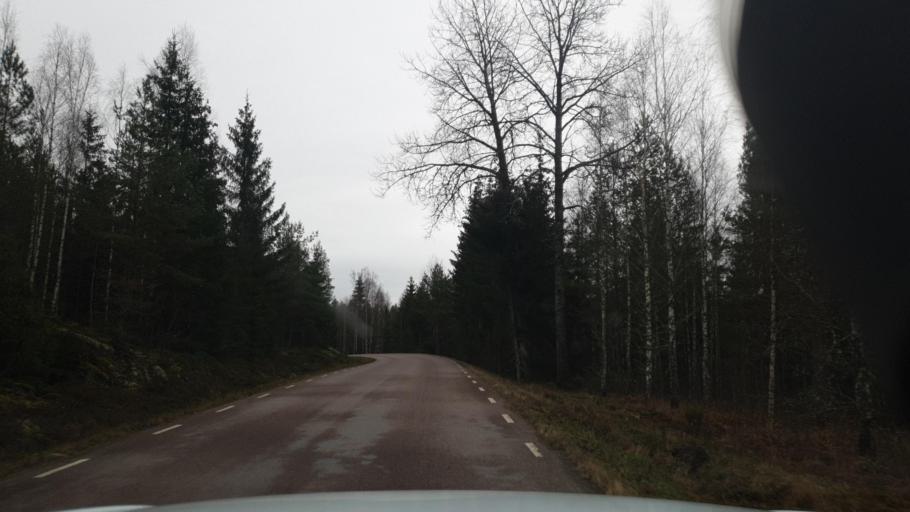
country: SE
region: Vaermland
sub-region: Karlstads Kommun
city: Valberg
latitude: 59.4576
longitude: 13.0837
